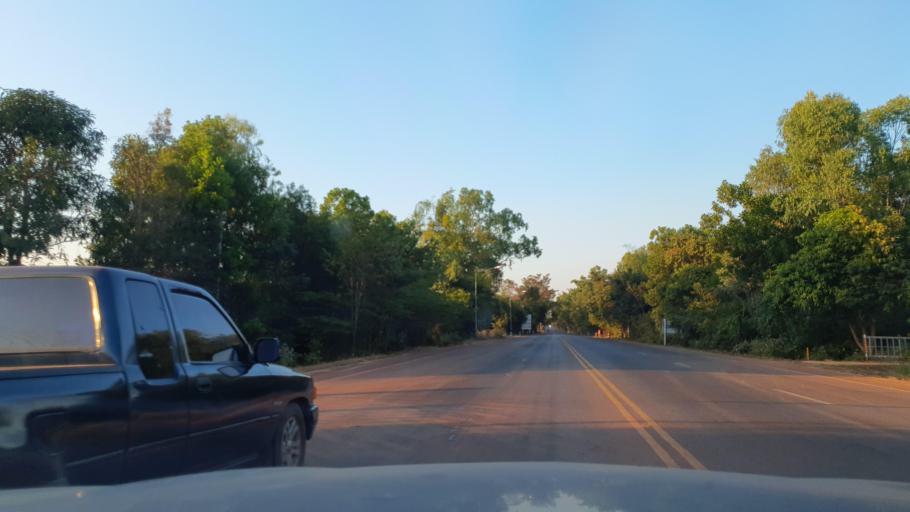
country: TH
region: Nakhon Phanom
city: Si Songkhram
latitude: 17.7669
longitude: 104.2780
